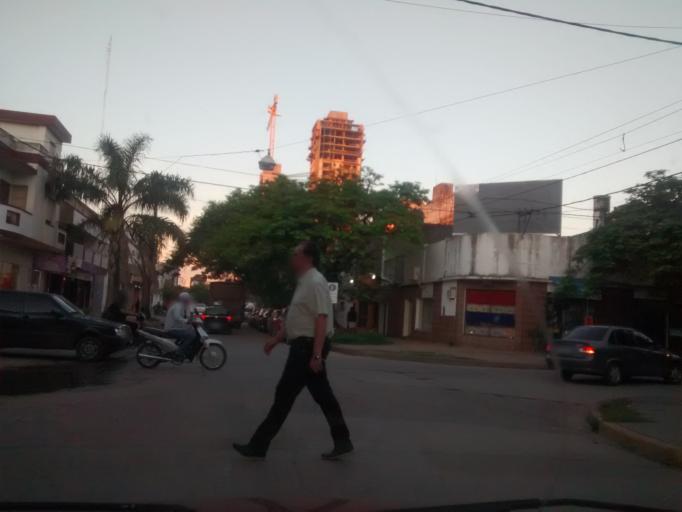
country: AR
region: Chaco
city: Resistencia
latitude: -27.4489
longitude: -58.9909
